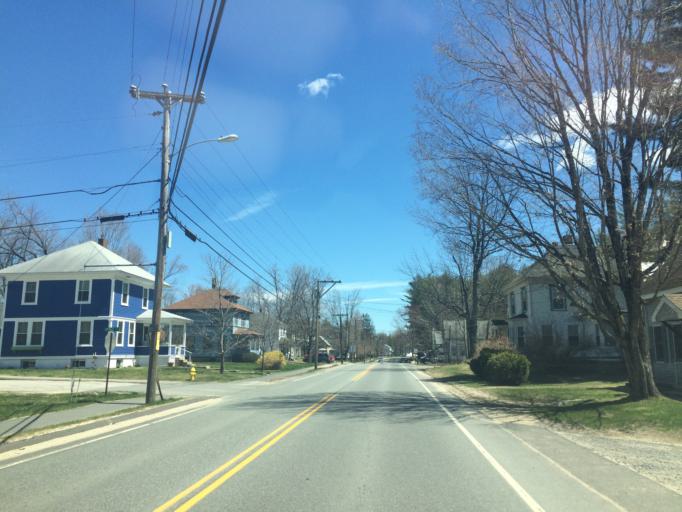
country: US
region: Maine
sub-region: Oxford County
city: Porter
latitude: 43.8067
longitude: -70.8823
